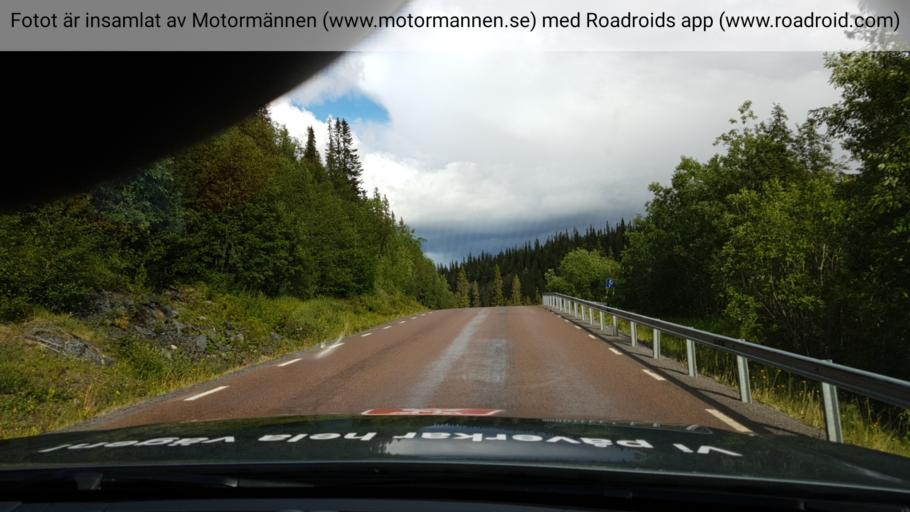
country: SE
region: Jaemtland
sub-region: Are Kommun
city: Jarpen
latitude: 63.1048
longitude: 13.8121
